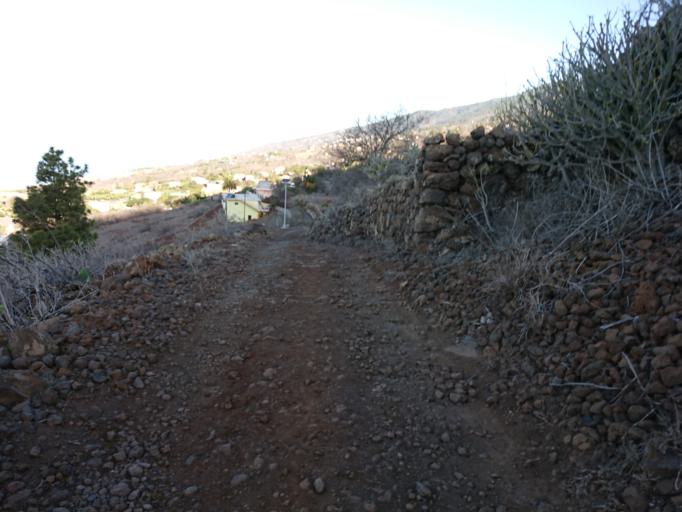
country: ES
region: Canary Islands
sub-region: Provincia de Santa Cruz de Tenerife
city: Los Llanos de Aridane
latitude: 28.6726
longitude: -17.9419
